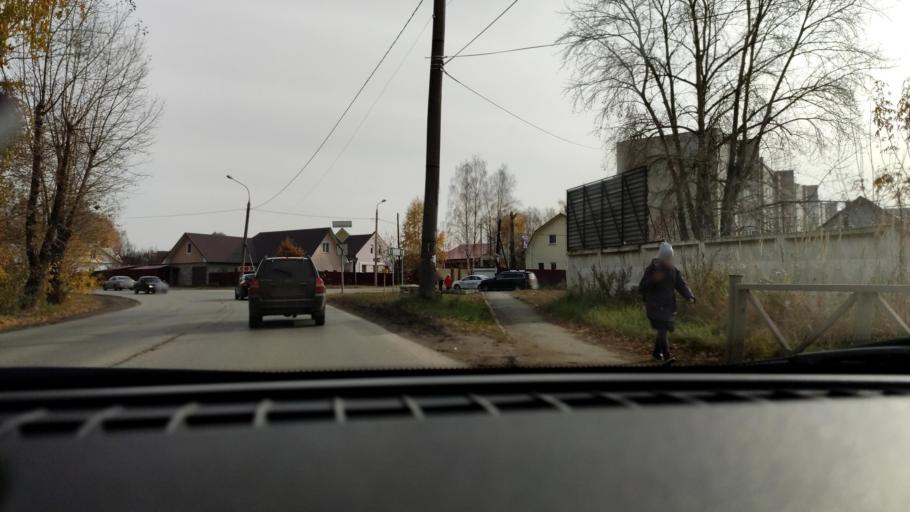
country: RU
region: Perm
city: Polazna
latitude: 58.1301
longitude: 56.3887
